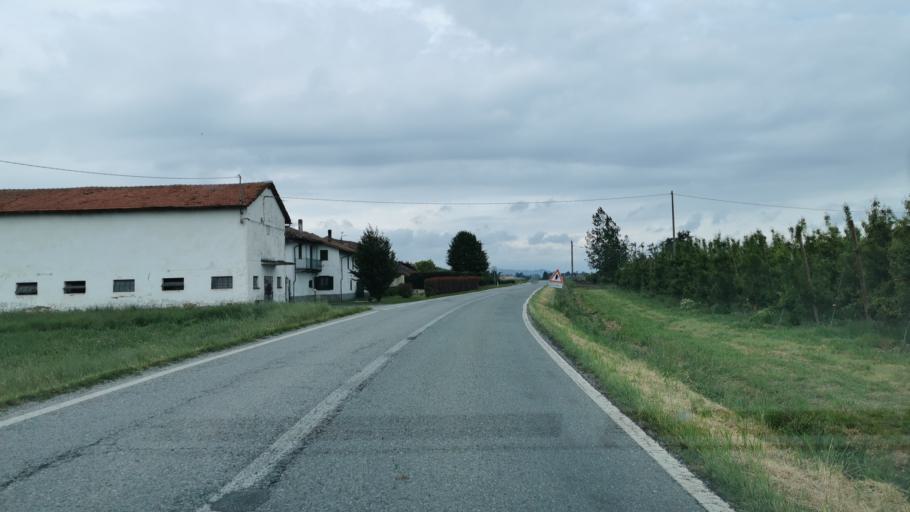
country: IT
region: Piedmont
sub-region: Provincia di Cuneo
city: Lagnasco
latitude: 44.6050
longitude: 7.5925
